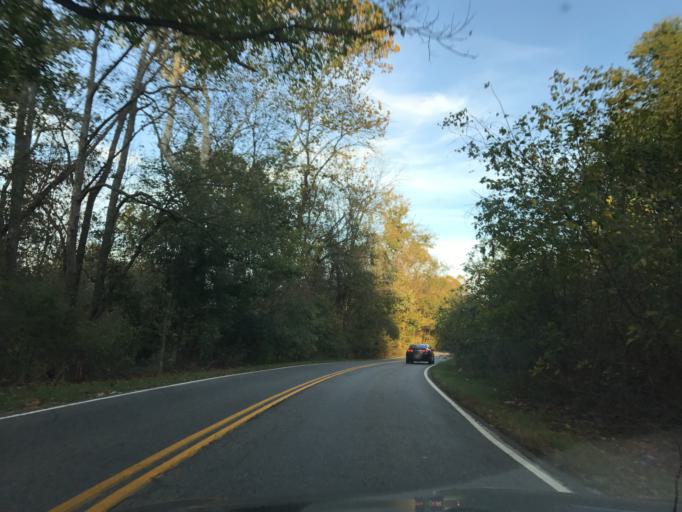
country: US
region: Maryland
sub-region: Prince George's County
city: South Laurel
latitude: 39.0719
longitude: -76.8375
